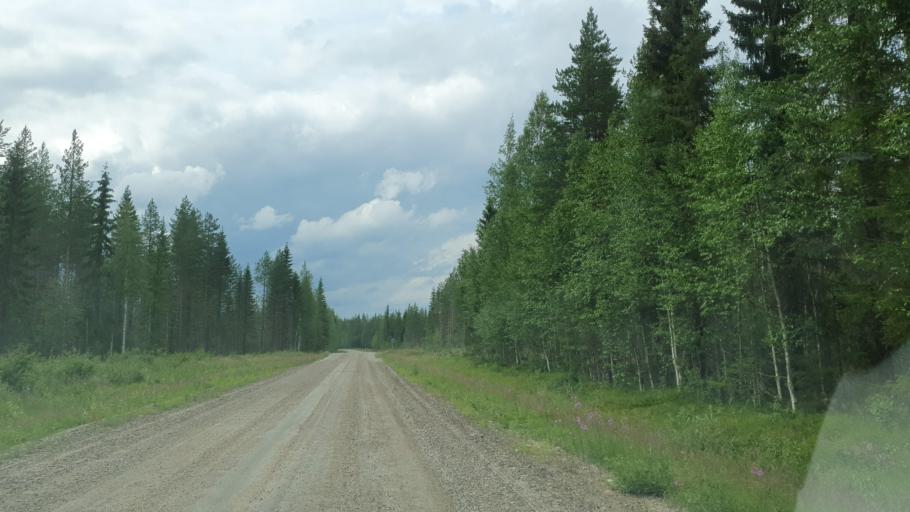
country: FI
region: Kainuu
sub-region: Kehys-Kainuu
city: Kuhmo
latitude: 64.4920
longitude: 29.6886
